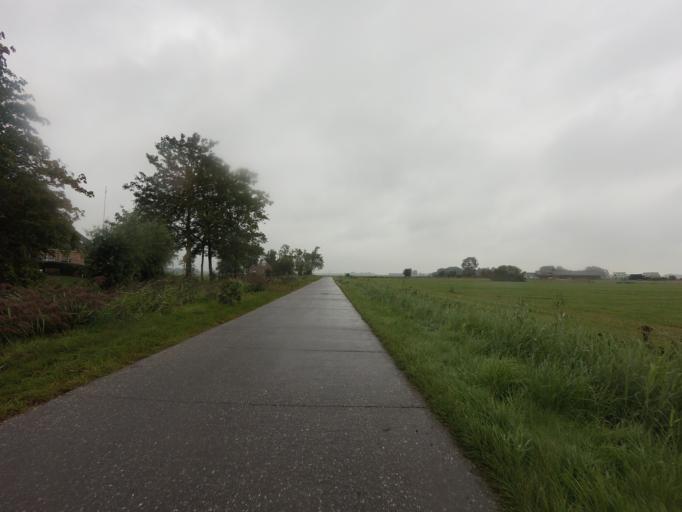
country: NL
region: Friesland
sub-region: Gemeente Boarnsterhim
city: Nes
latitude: 53.0289
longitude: 5.8646
